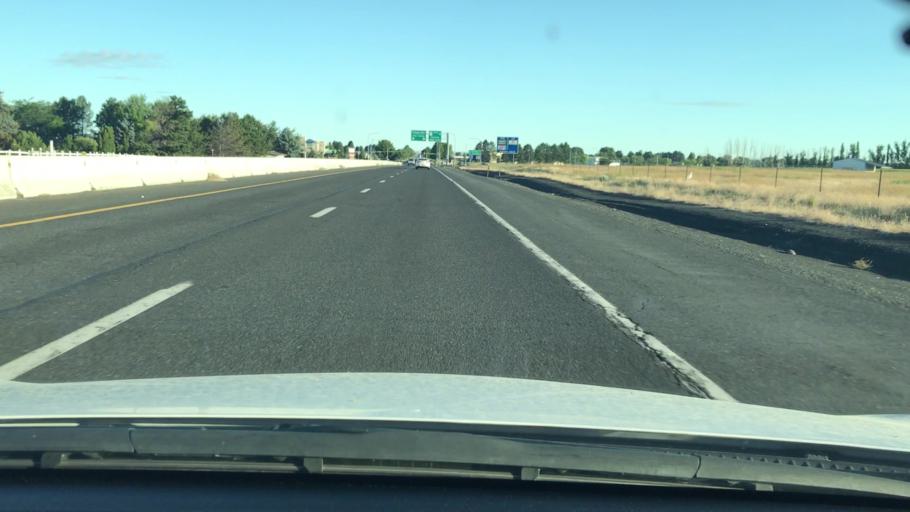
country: US
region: Washington
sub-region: Grant County
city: Moses Lake
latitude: 47.1079
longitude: -119.2538
